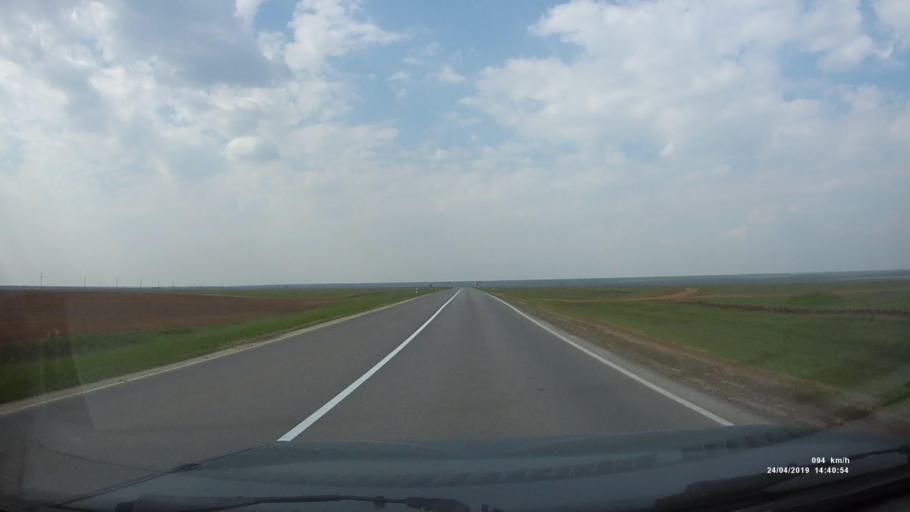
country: RU
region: Rostov
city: Remontnoye
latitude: 46.4387
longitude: 43.8848
